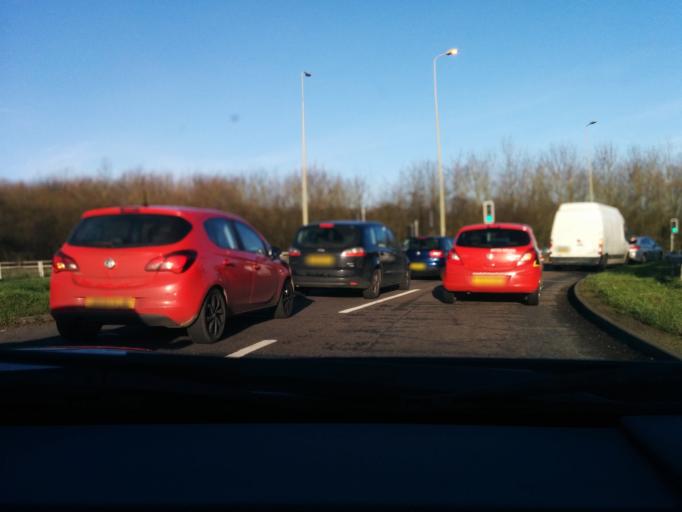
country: GB
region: England
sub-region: Oxfordshire
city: Boars Hill
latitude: 51.7559
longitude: -1.2973
